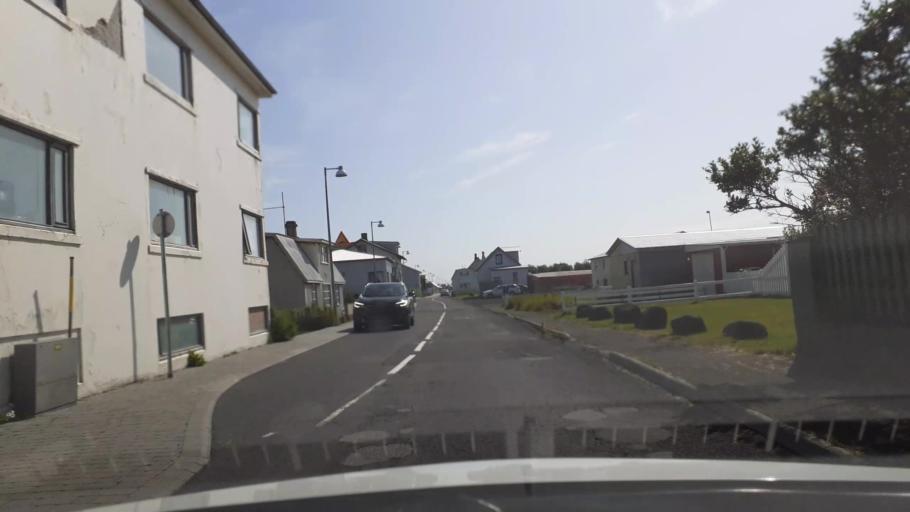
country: IS
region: South
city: Hveragerdi
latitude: 63.8640
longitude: -21.1534
